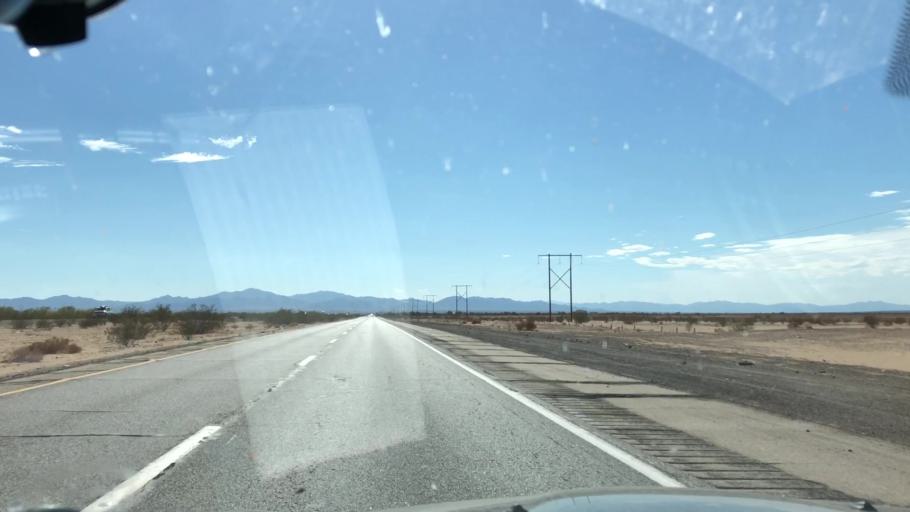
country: US
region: California
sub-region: Riverside County
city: Mesa Verde
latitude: 33.6063
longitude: -114.9566
